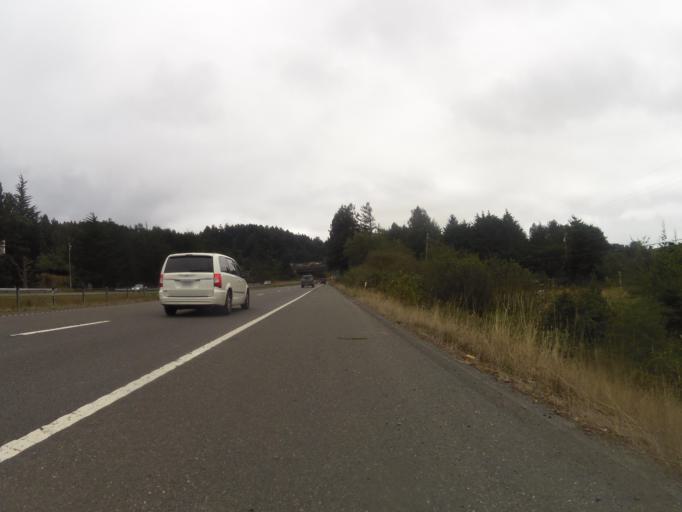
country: US
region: California
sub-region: Humboldt County
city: Arcata
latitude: 40.8896
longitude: -124.0801
